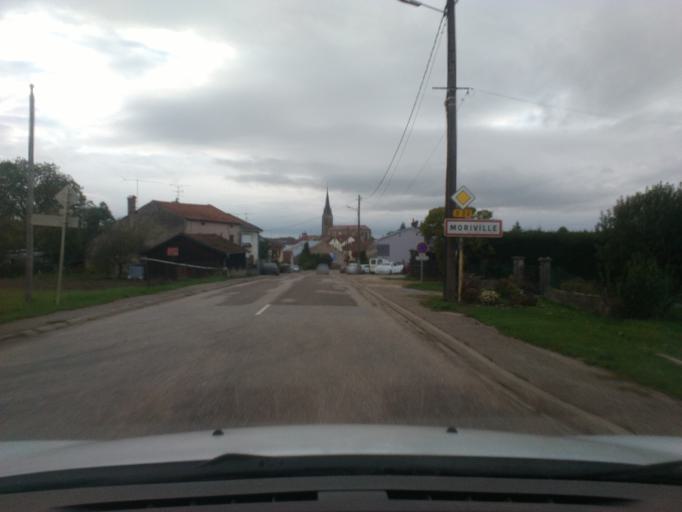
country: FR
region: Lorraine
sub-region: Departement des Vosges
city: Chatel-sur-Moselle
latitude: 48.3461
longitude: 6.4374
